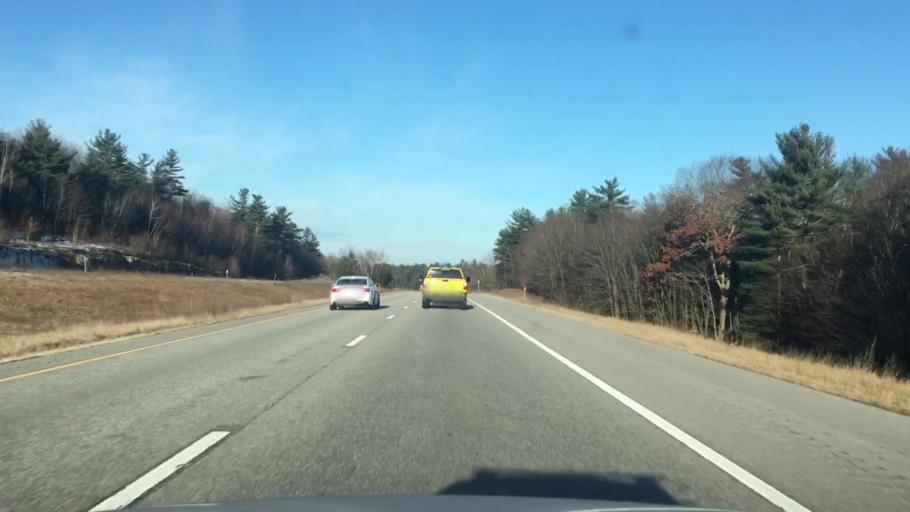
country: US
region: New Hampshire
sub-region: Rockingham County
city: Candia
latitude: 43.0390
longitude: -71.2619
